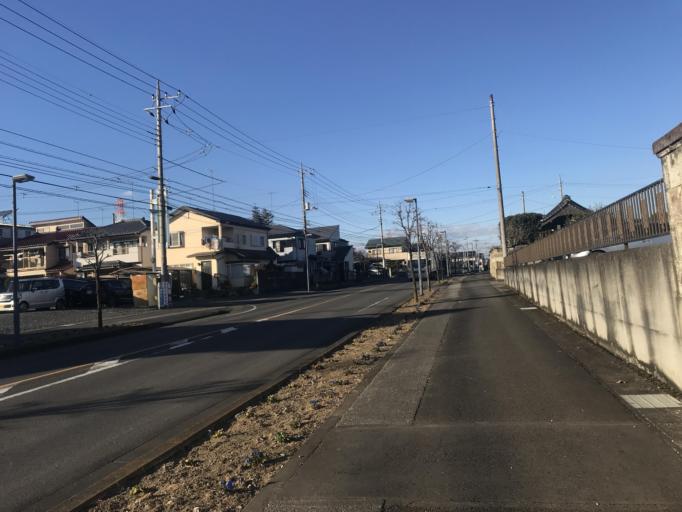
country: JP
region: Tochigi
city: Kaminokawa
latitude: 36.4349
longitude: 139.8714
